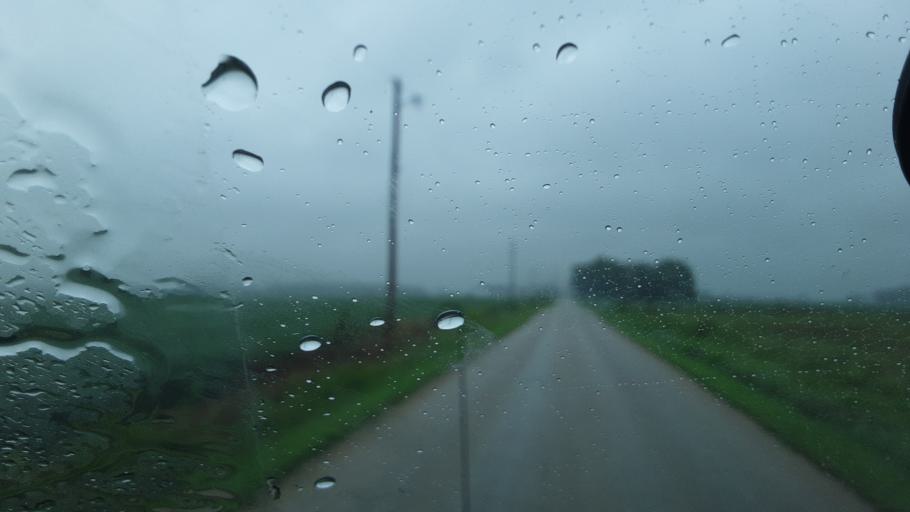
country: US
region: Indiana
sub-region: Adams County
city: Berne
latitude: 40.6746
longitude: -84.8203
